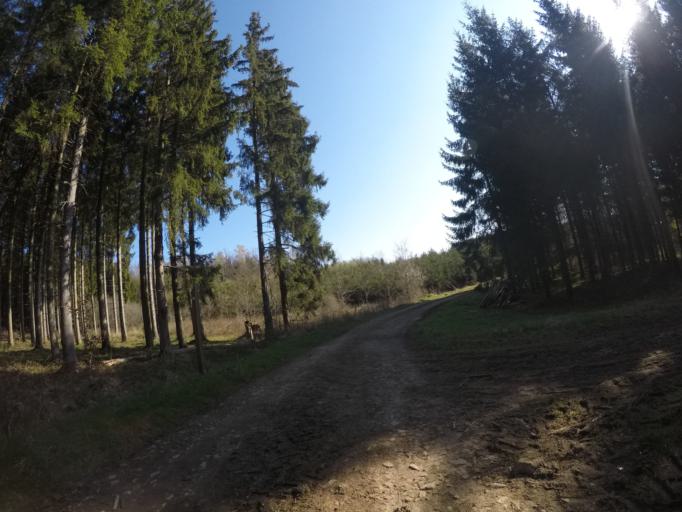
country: BE
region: Wallonia
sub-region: Province du Luxembourg
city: Leglise
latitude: 49.7848
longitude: 5.5878
